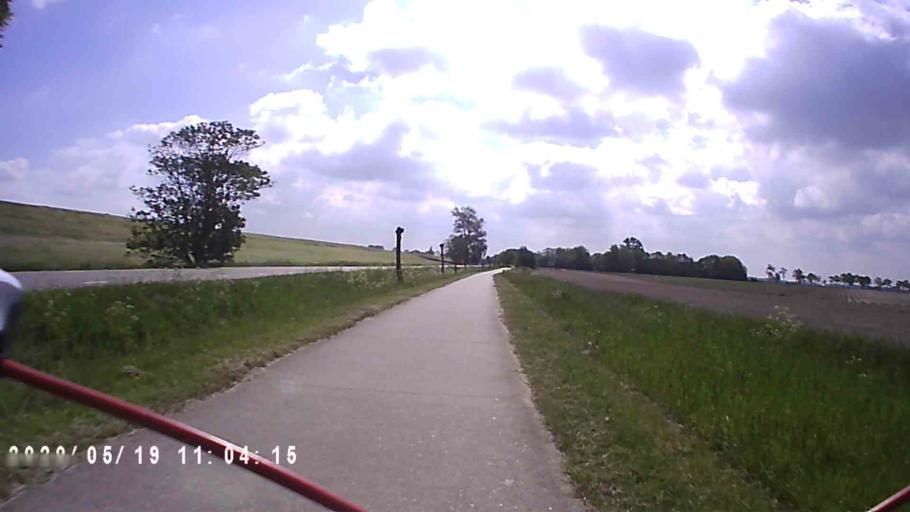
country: NL
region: Groningen
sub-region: Gemeente Zuidhorn
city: Grijpskerk
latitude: 53.2976
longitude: 6.2839
